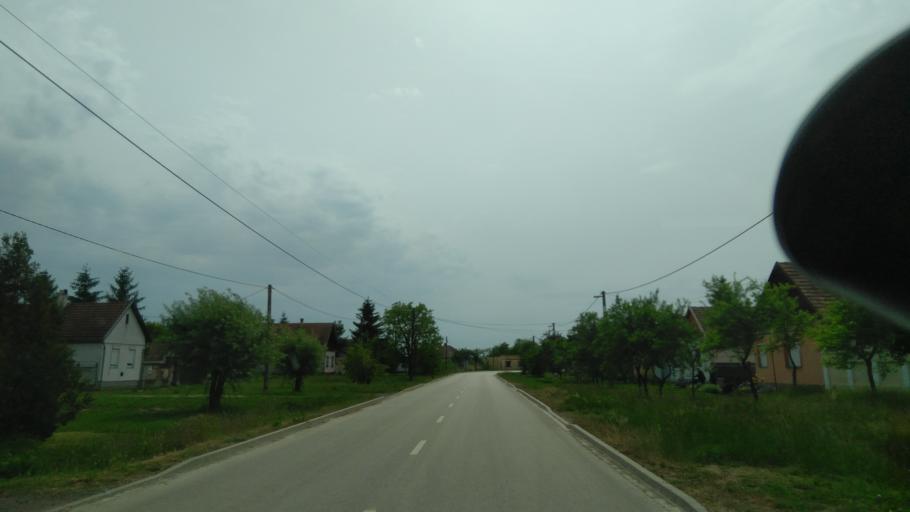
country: HU
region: Bekes
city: Mehkerek
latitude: 46.8674
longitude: 21.5203
